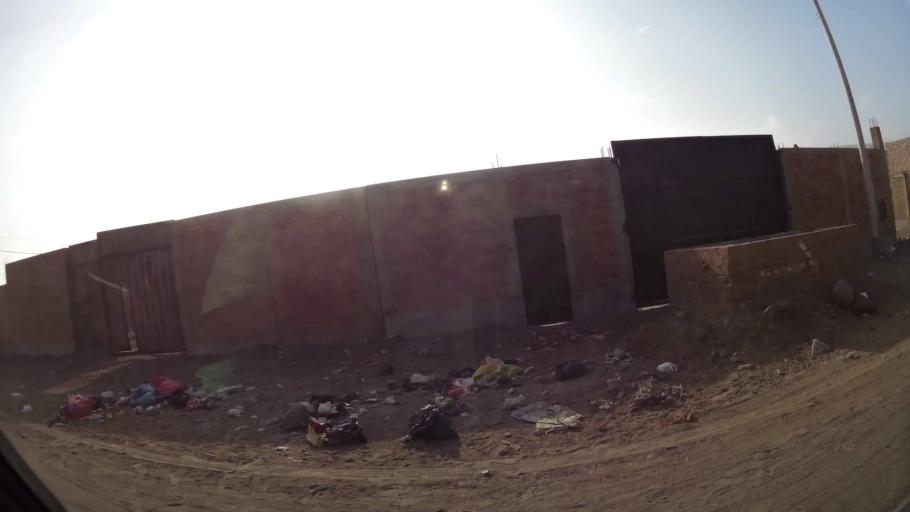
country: PE
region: Lima
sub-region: Lima
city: Santa Rosa
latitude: -11.7551
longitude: -77.1582
